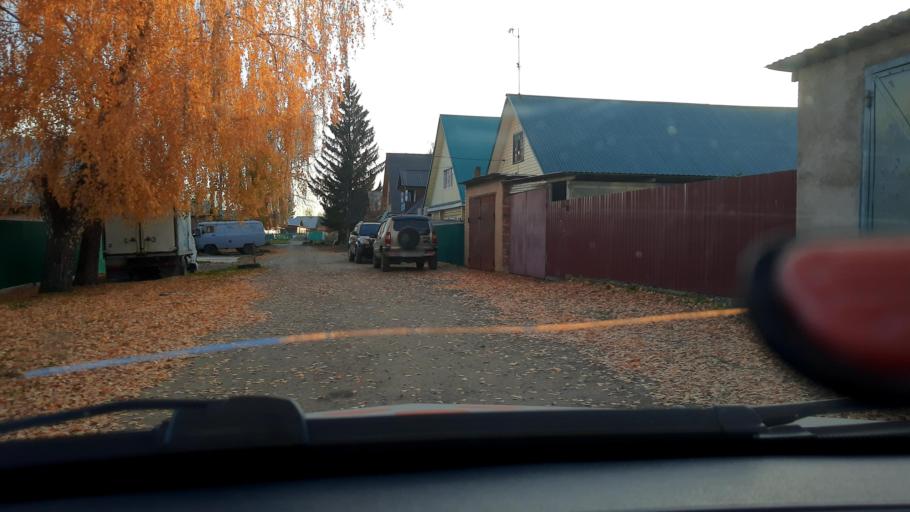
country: RU
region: Bashkortostan
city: Ufa
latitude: 54.8158
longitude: 56.1611
